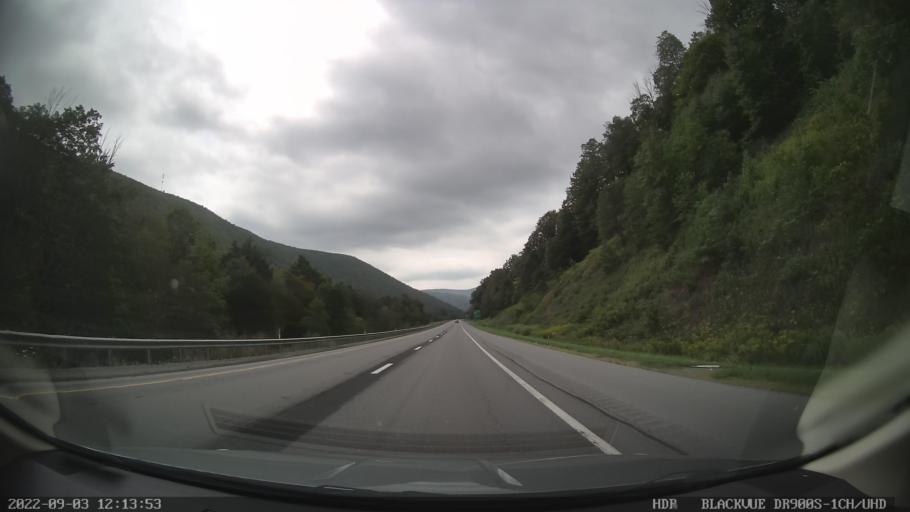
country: US
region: Pennsylvania
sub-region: Lycoming County
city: Garden View
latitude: 41.4115
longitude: -77.0677
